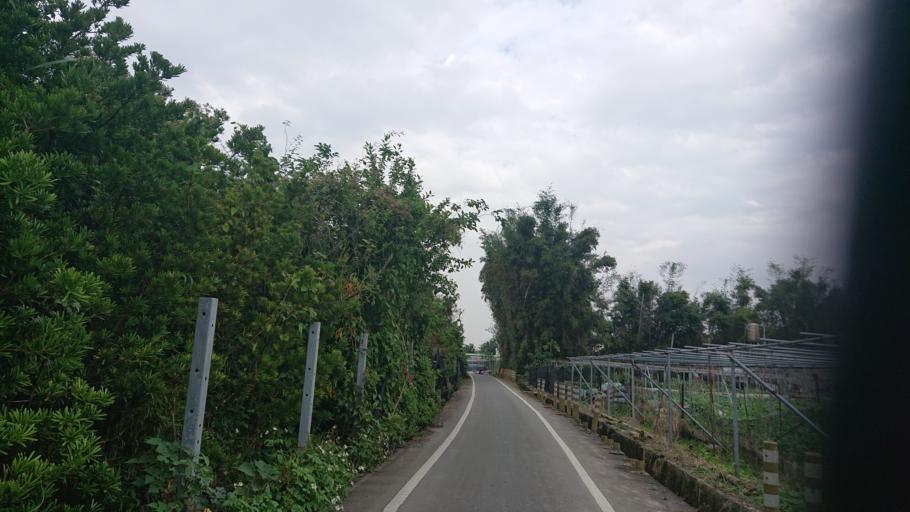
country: TW
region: Taiwan
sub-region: Taoyuan
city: Taoyuan
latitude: 24.9524
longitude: 121.3696
